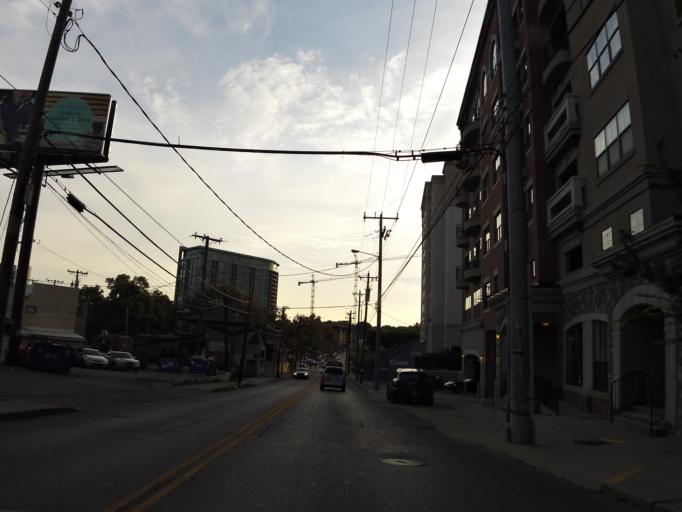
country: US
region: Tennessee
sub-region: Davidson County
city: Nashville
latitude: 36.1512
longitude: -86.7946
